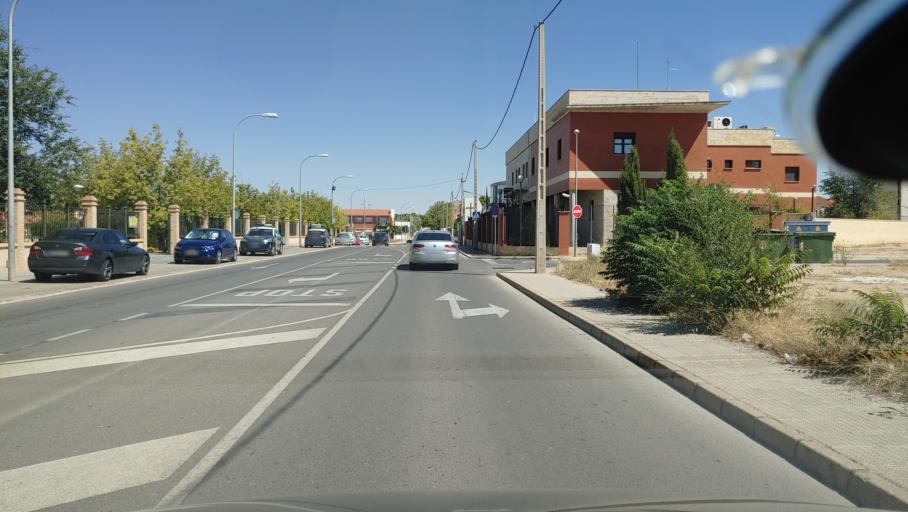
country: ES
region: Castille-La Mancha
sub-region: Provincia de Ciudad Real
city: Valdepenas
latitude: 38.7707
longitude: -3.3874
